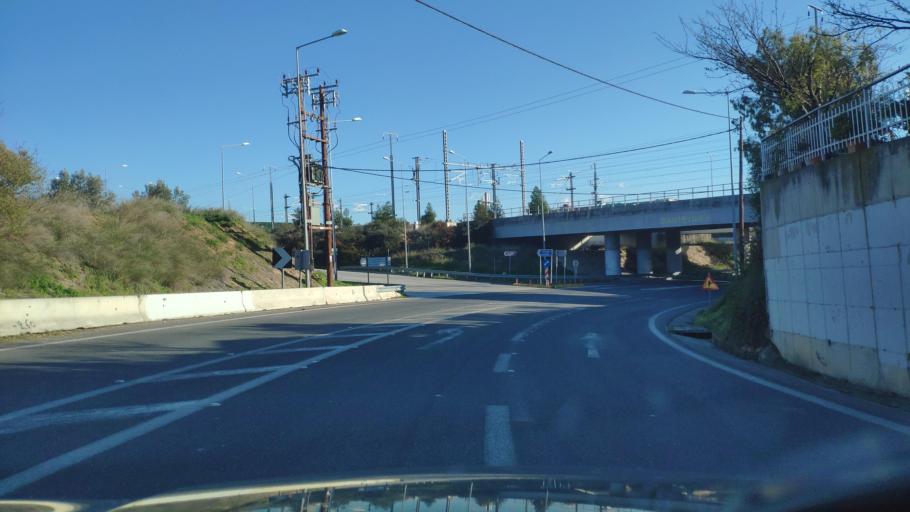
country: GR
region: Peloponnese
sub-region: Nomos Korinthias
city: Korinthos
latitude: 37.9222
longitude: 22.9368
